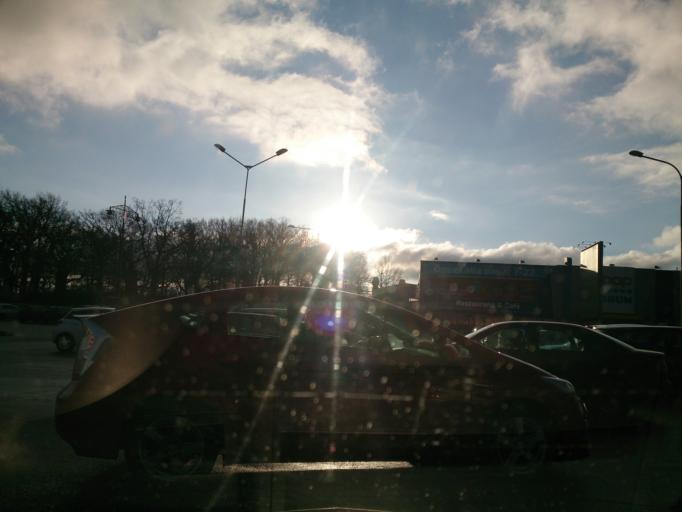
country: SE
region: OEstergoetland
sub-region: Norrkopings Kommun
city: Norrkoping
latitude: 58.6166
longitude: 16.1633
